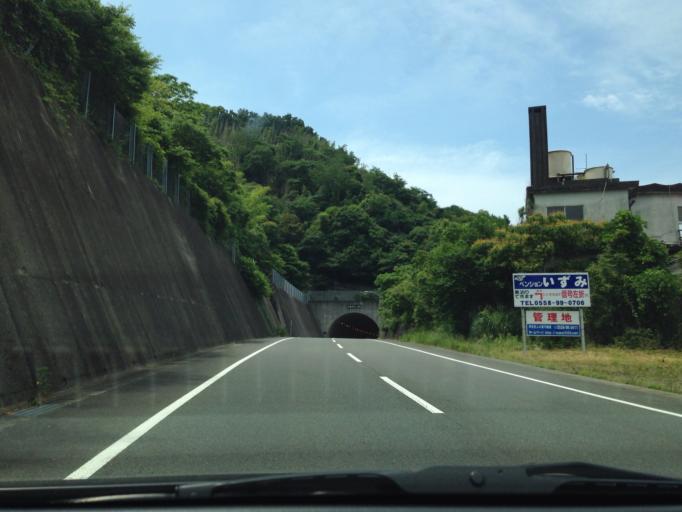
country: JP
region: Shizuoka
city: Heda
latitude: 34.8982
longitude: 138.7792
